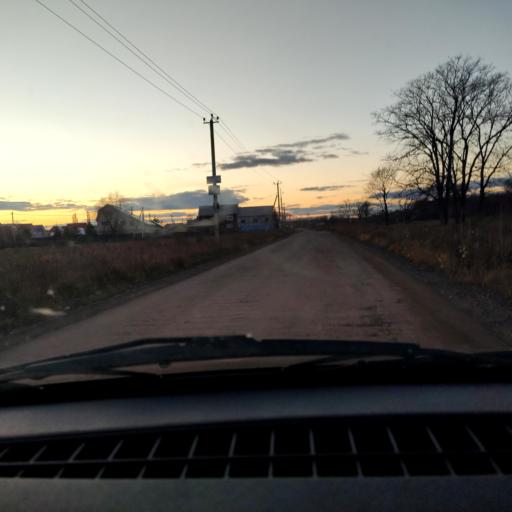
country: RU
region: Bashkortostan
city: Ufa
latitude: 54.6453
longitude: 55.9116
